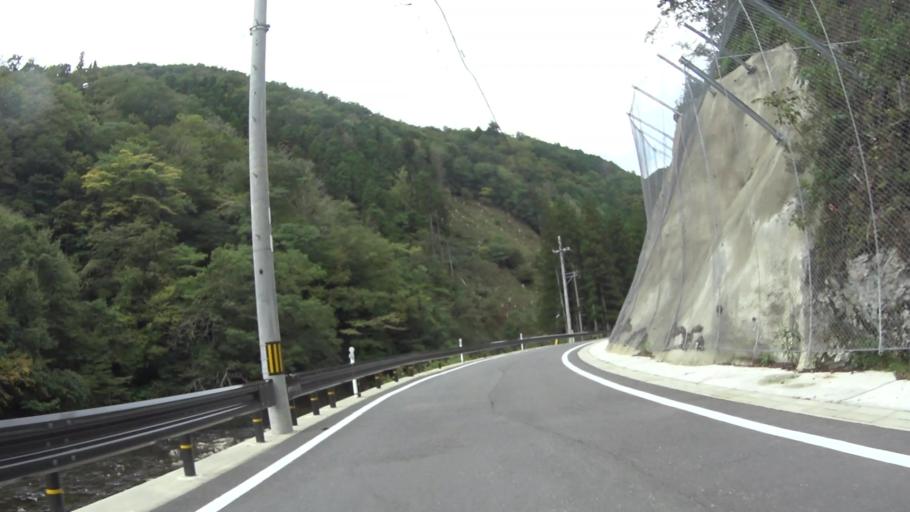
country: JP
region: Fukui
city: Obama
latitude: 35.2875
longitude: 135.6973
